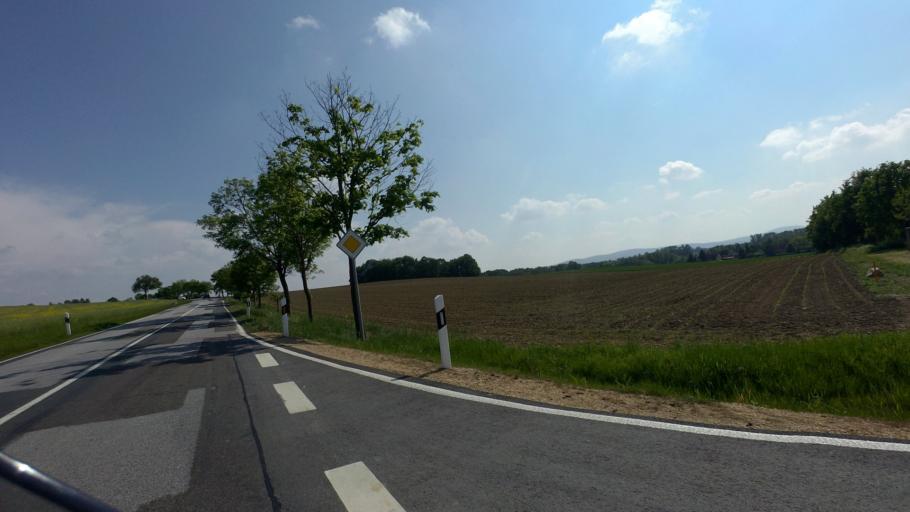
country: DE
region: Saxony
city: Weissenberg
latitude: 51.1810
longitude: 14.6451
